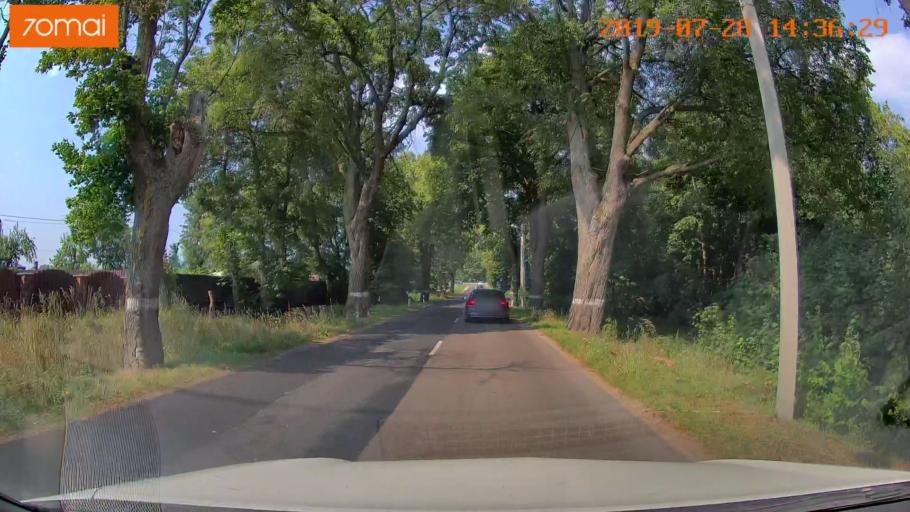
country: RU
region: Kaliningrad
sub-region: Gorod Kaliningrad
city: Yantarnyy
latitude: 54.8379
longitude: 20.0075
